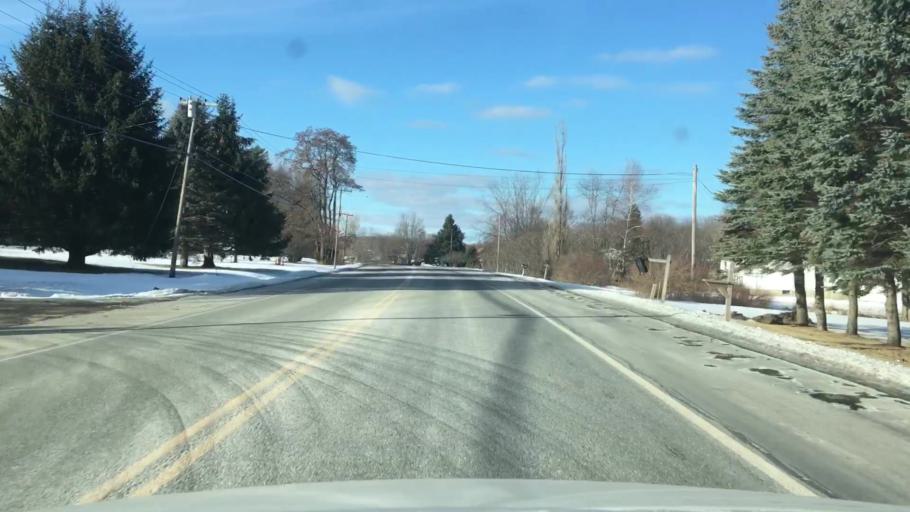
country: US
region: Maine
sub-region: Penobscot County
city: Eddington
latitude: 44.8214
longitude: -68.6493
